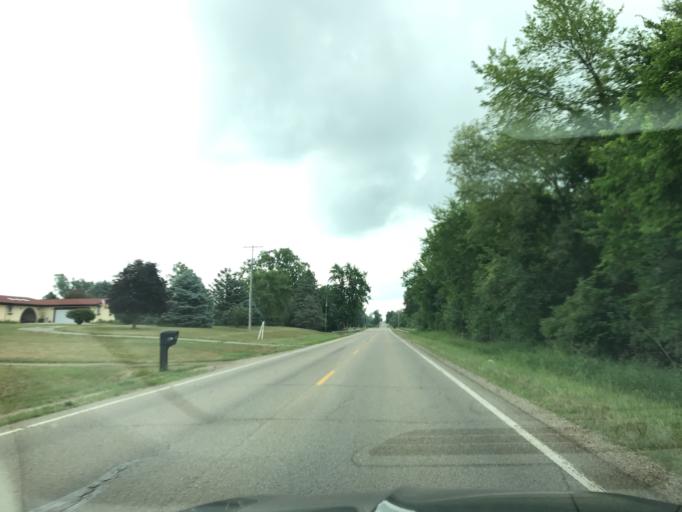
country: US
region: Michigan
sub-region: Eaton County
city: Grand Ledge
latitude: 42.8007
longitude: -84.7534
